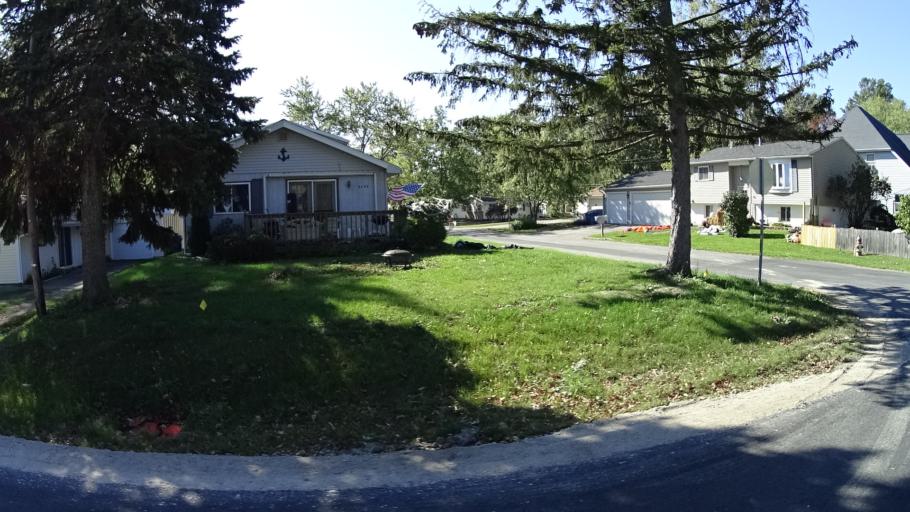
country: US
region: Ohio
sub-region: Lorain County
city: Vermilion-on-the-Lake
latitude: 41.4298
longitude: -82.3167
